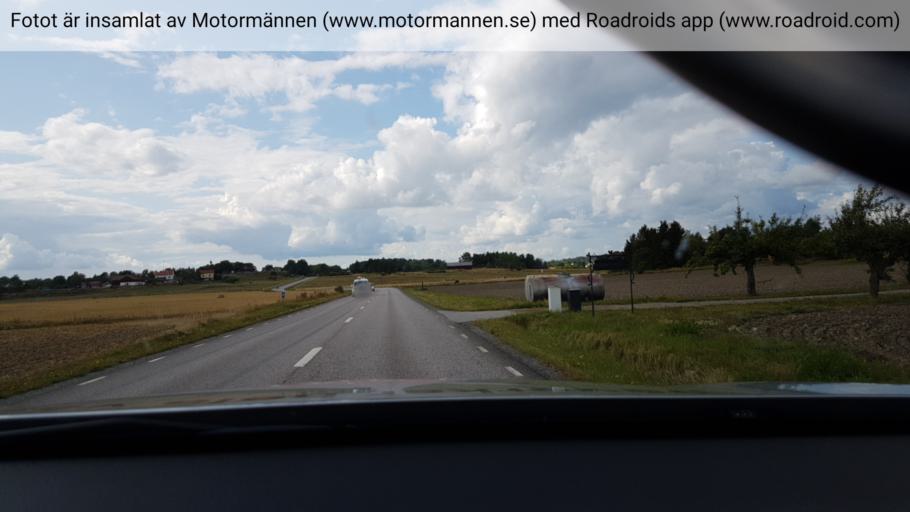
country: SE
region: Stockholm
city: Stenhamra
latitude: 59.3893
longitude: 17.6738
